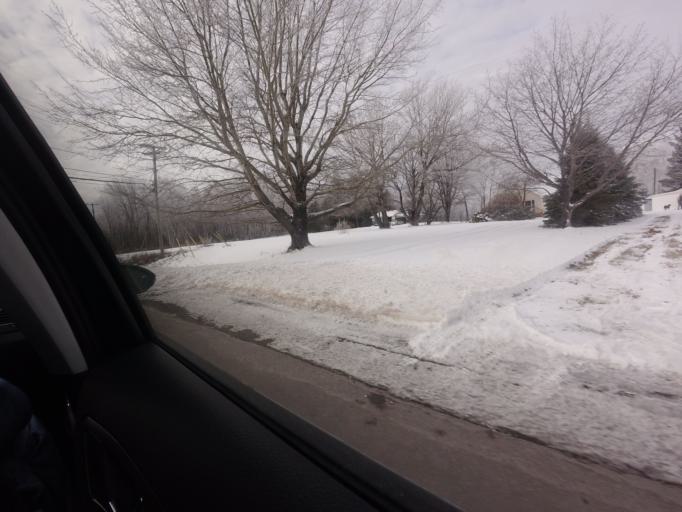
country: CA
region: New Brunswick
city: Oromocto
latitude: 45.8602
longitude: -66.4506
